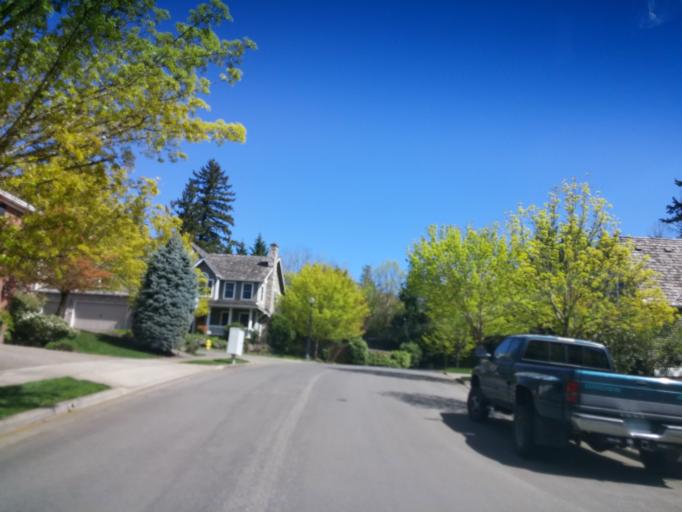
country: US
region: Oregon
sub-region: Washington County
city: West Haven
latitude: 45.5315
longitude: -122.7702
